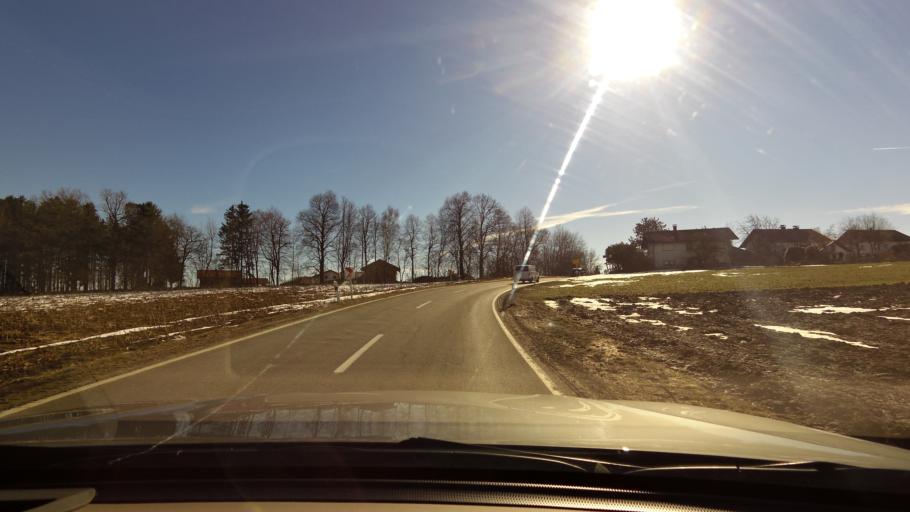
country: DE
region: Bavaria
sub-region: Upper Bavaria
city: Taufkirchen
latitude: 48.1312
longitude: 12.4614
